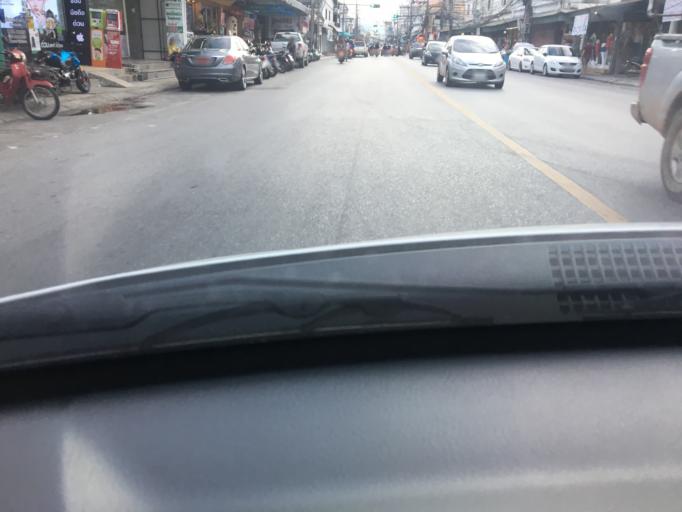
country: TH
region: Phuket
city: Ban Talat Yai
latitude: 7.8772
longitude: 98.3943
